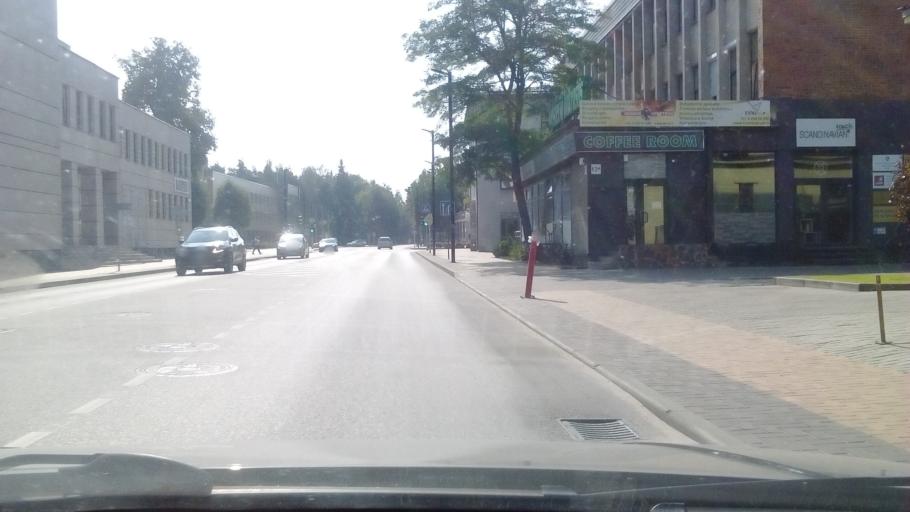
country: LT
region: Alytaus apskritis
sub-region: Alytus
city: Alytus
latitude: 54.3970
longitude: 24.0462
